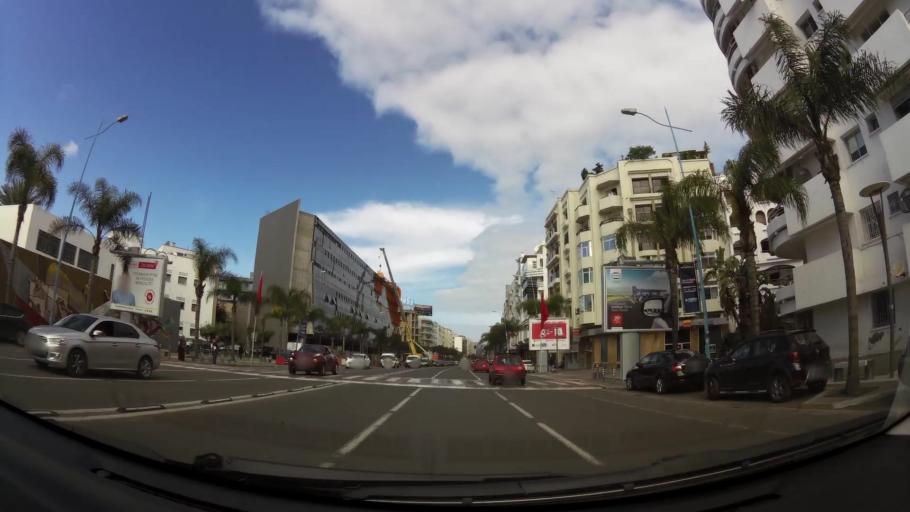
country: MA
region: Grand Casablanca
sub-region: Casablanca
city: Casablanca
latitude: 33.5868
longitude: -7.6375
